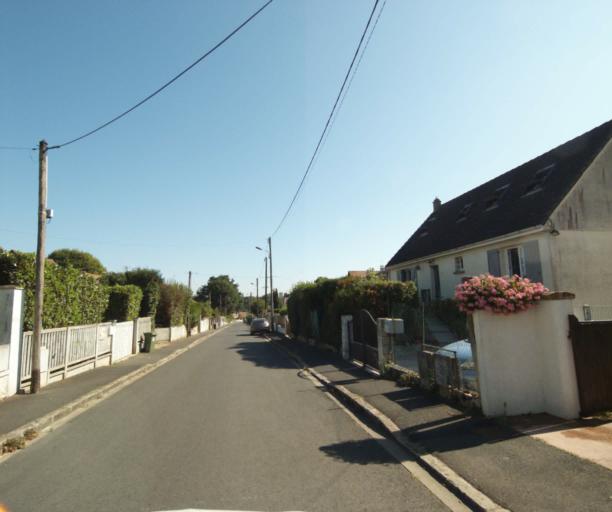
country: FR
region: Ile-de-France
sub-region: Departement de l'Essonne
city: Saint-Vrain
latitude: 48.5335
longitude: 2.3497
